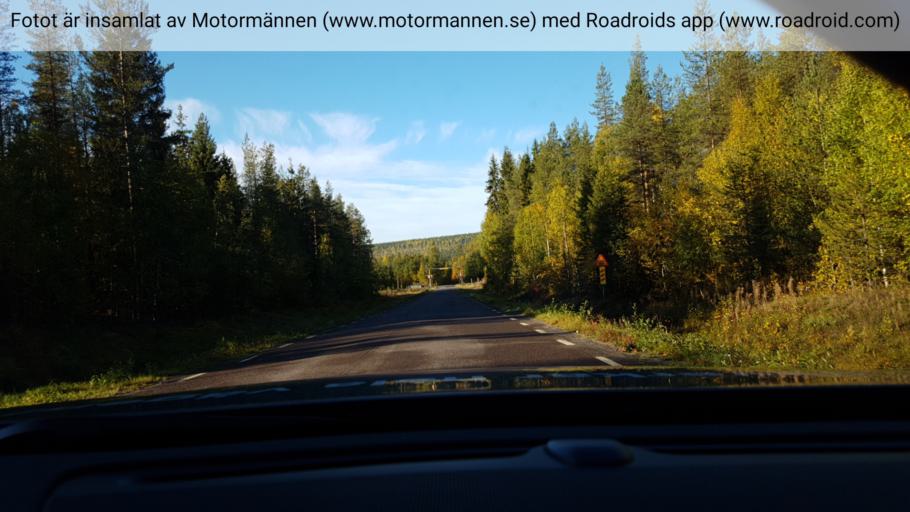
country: SE
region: Norrbotten
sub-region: Bodens Kommun
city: Boden
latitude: 66.0594
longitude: 21.4210
